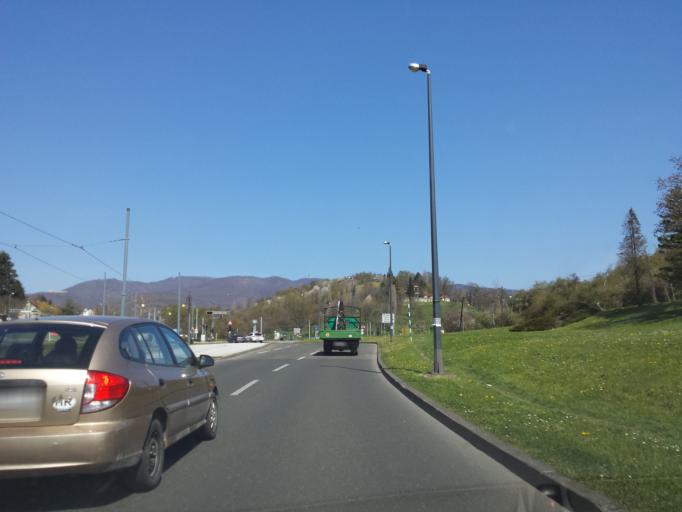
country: HR
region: Grad Zagreb
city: Zagreb
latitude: 45.8403
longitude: 15.9759
